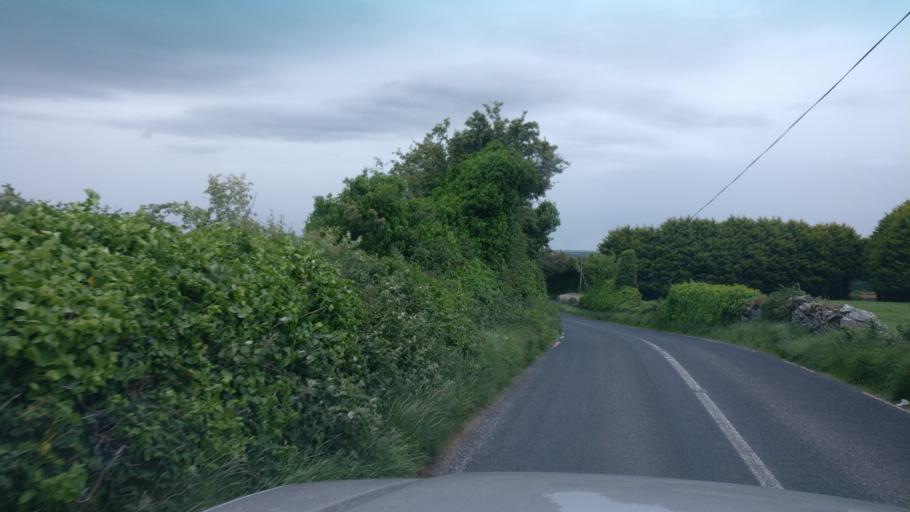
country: IE
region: Connaught
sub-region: County Galway
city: Loughrea
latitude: 53.0956
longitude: -8.4336
